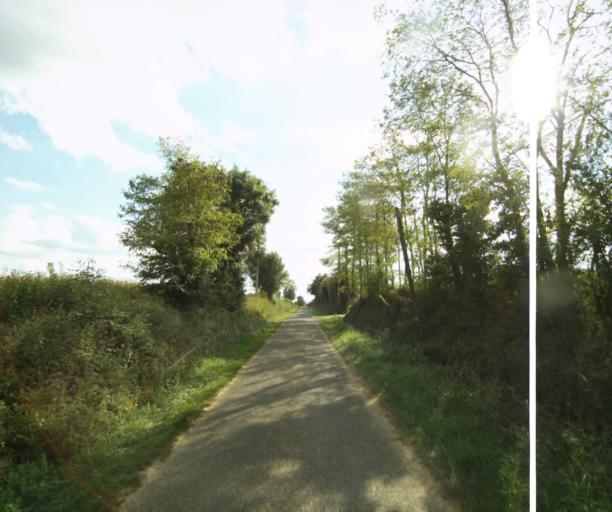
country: FR
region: Midi-Pyrenees
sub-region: Departement du Gers
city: Cazaubon
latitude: 43.8806
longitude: -0.0429
